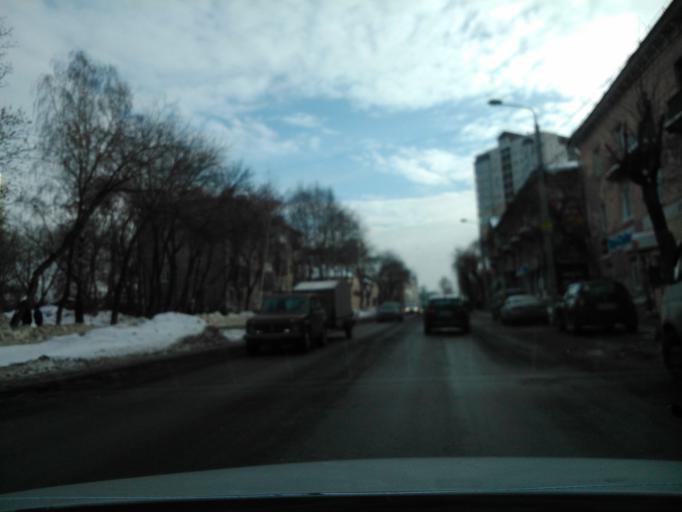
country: RU
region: Perm
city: Perm
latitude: 58.0009
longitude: 56.2399
